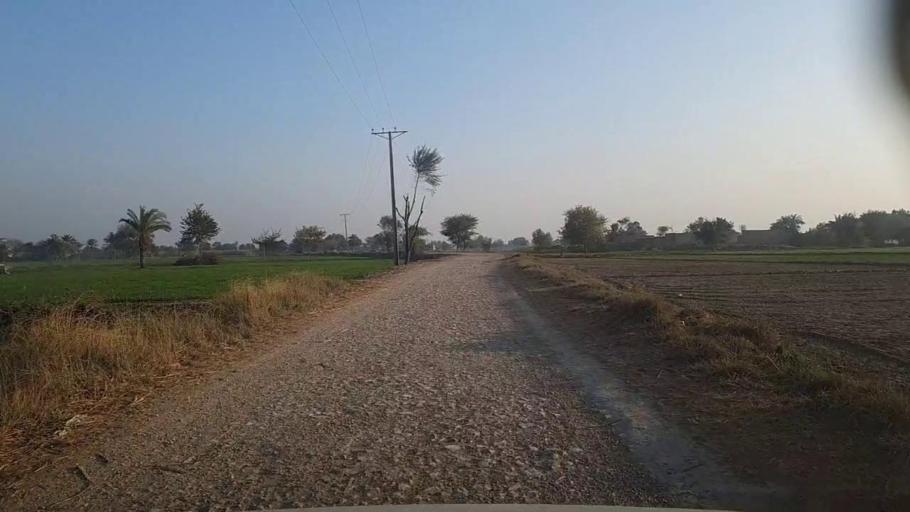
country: PK
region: Sindh
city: Khairpur
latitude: 28.0627
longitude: 69.7538
